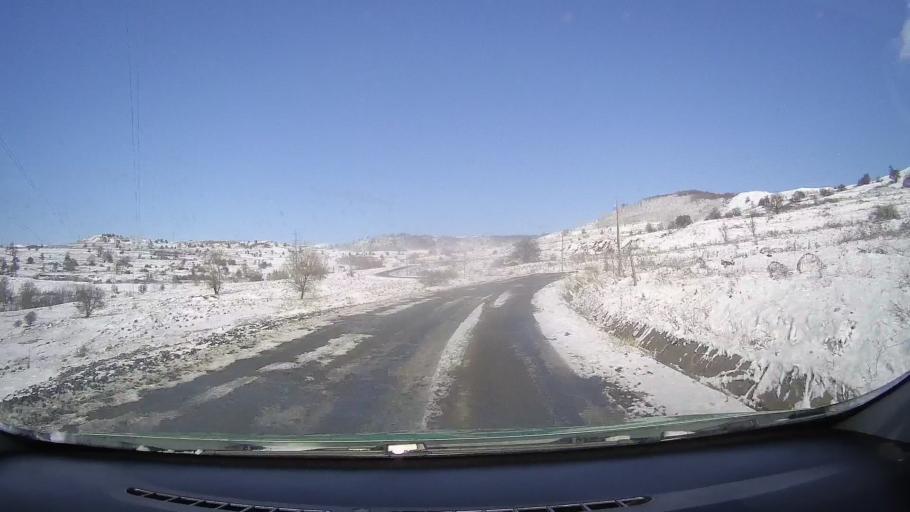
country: RO
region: Sibiu
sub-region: Comuna Avrig
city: Avrig
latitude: 45.7685
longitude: 24.3860
